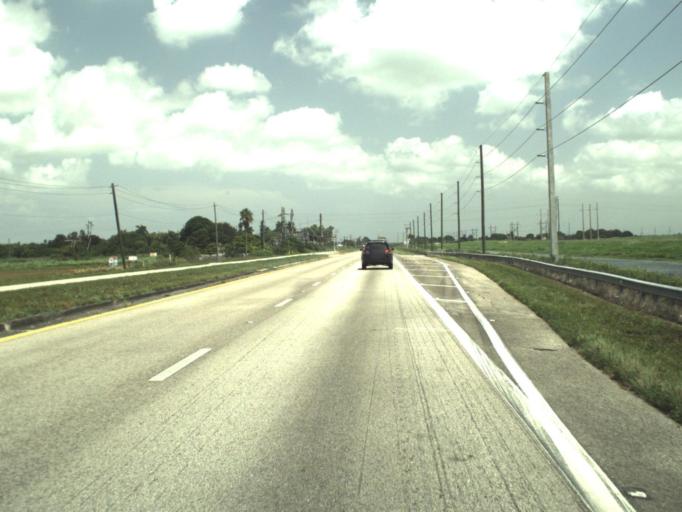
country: US
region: Florida
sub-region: Palm Beach County
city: South Bay
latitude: 26.6449
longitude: -80.7123
